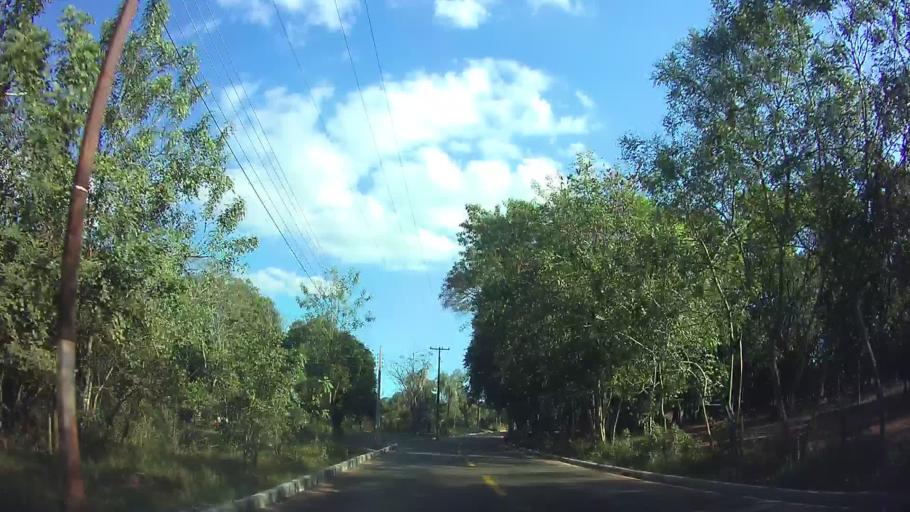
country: PY
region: Central
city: Aregua
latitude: -25.2727
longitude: -57.4388
